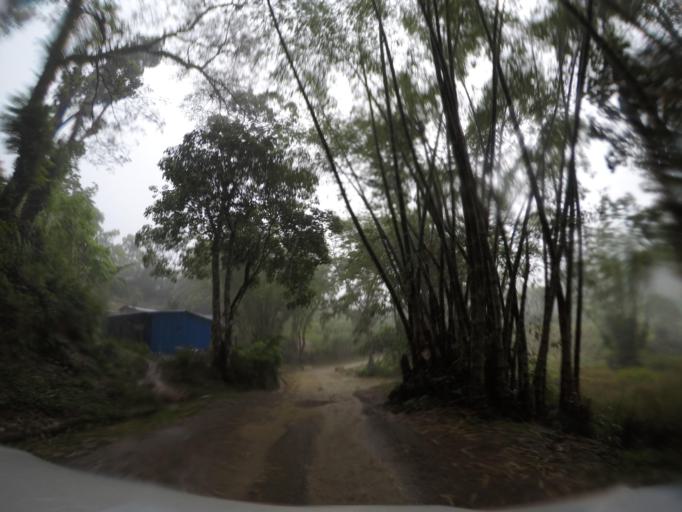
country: TL
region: Baucau
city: Venilale
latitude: -8.6433
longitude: 126.4010
